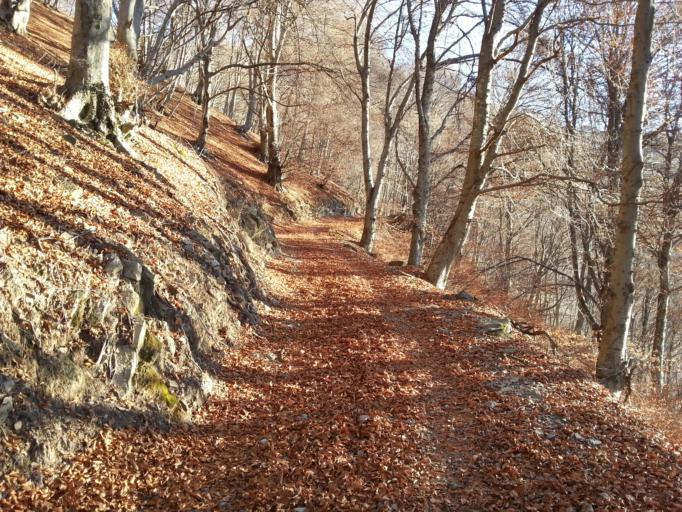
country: CH
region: Ticino
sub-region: Lugano District
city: Cadro
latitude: 46.0240
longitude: 9.0010
